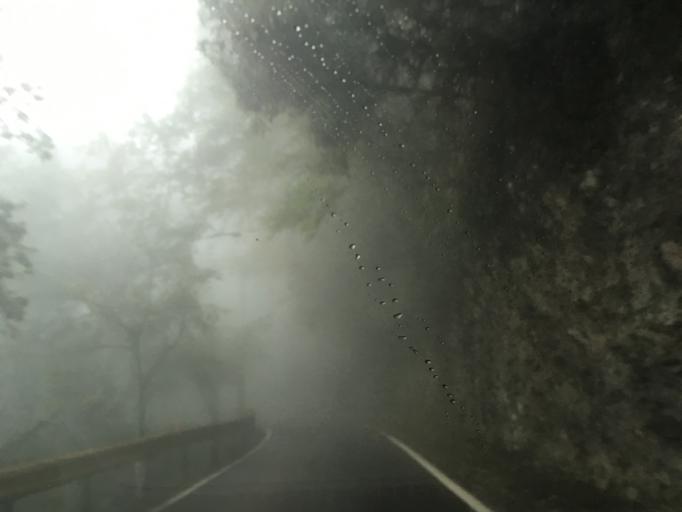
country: TW
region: Taiwan
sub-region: Hualien
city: Hualian
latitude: 24.1903
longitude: 121.4202
